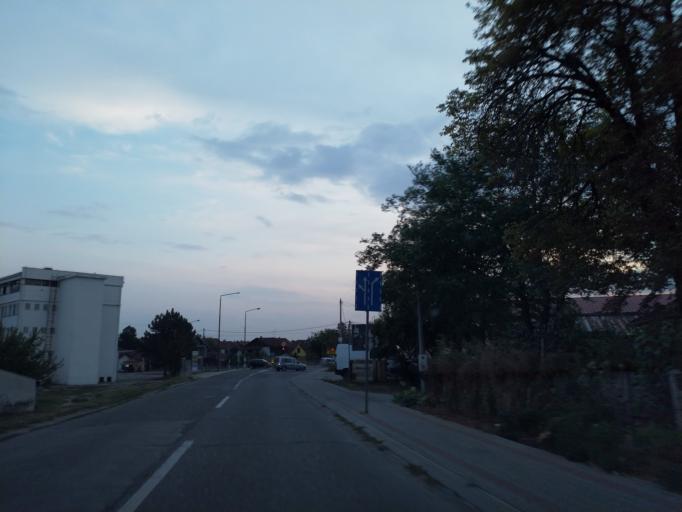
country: RS
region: Central Serbia
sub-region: Pomoravski Okrug
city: Paracin
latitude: 43.8664
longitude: 21.4213
